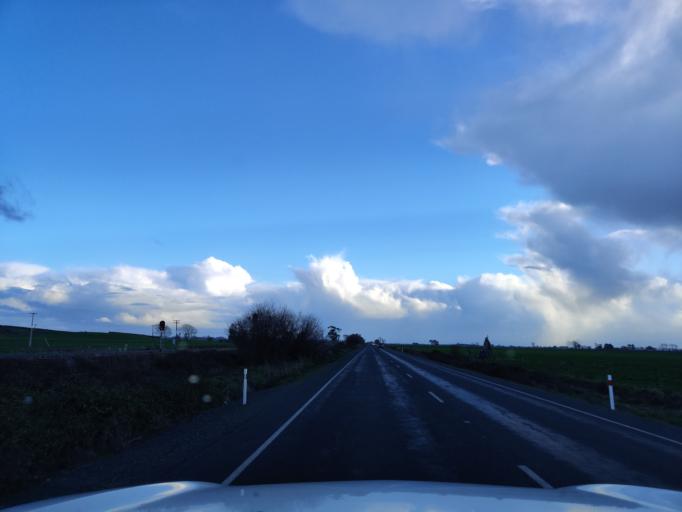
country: NZ
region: Waikato
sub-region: Waipa District
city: Cambridge
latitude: -37.6804
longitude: 175.4572
